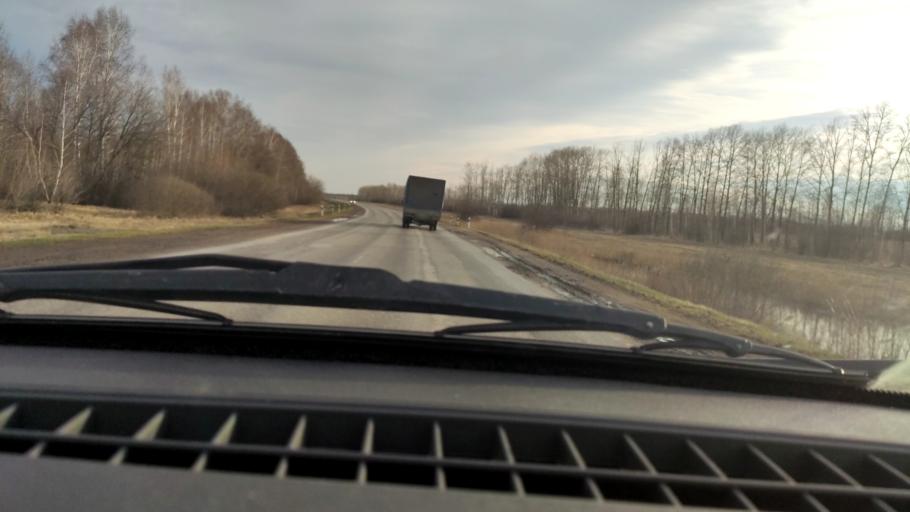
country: RU
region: Bashkortostan
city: Davlekanovo
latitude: 54.3500
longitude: 55.1783
